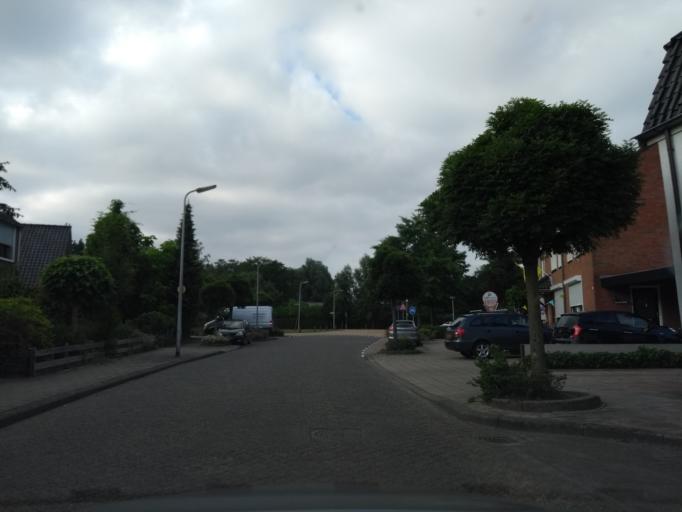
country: NL
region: Overijssel
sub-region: Gemeente Hof van Twente
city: Goor
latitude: 52.2368
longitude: 6.5830
